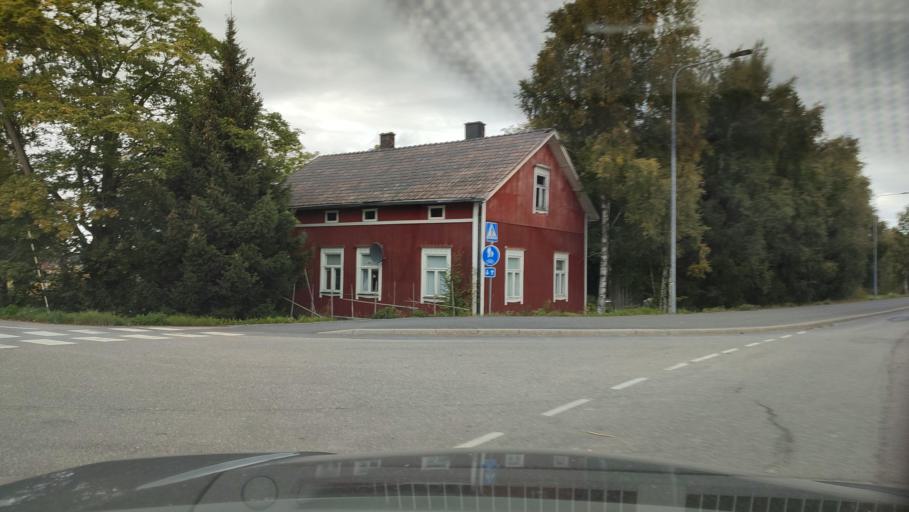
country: FI
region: Ostrobothnia
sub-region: Sydosterbotten
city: Kristinestad
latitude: 62.2572
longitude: 21.5269
